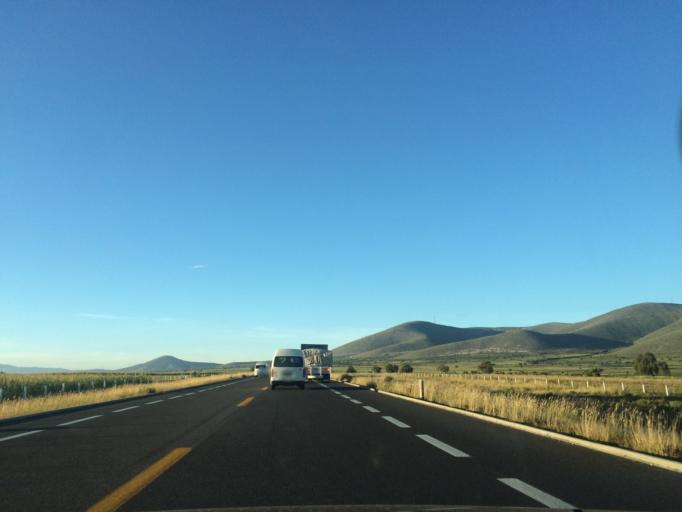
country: MX
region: Puebla
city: Morelos Canada
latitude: 18.7552
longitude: -97.4811
